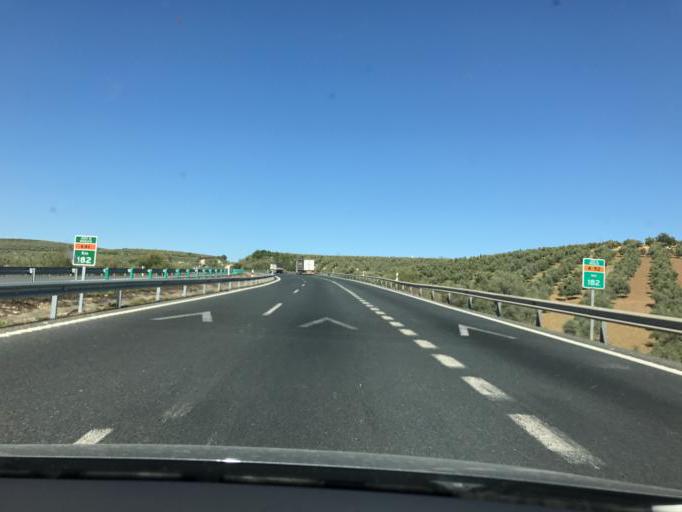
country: ES
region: Andalusia
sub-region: Provincia de Granada
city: Loja
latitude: 37.1457
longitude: -4.2393
